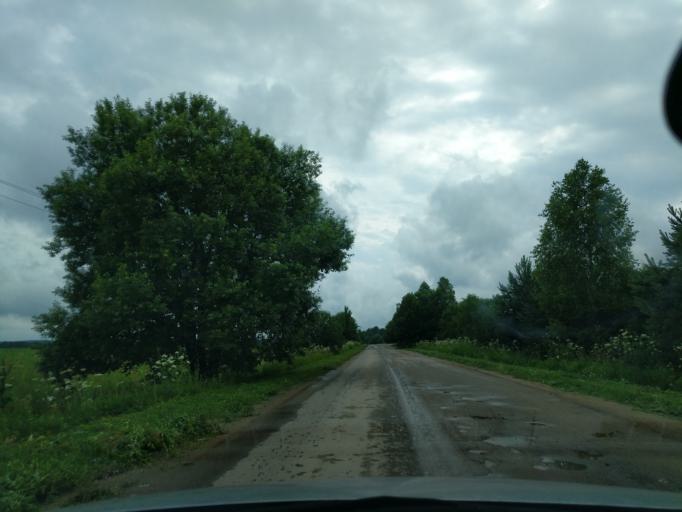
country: RU
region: Kaluga
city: Nikola-Lenivets
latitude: 54.7757
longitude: 35.7205
